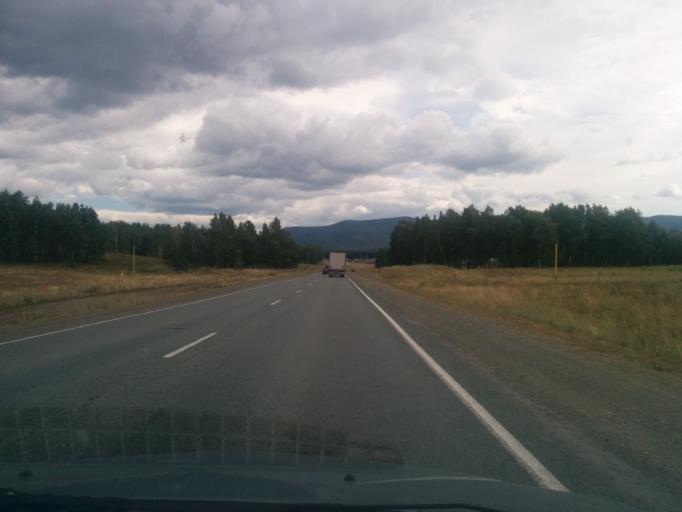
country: RU
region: Bashkortostan
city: Lomovka
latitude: 53.8896
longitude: 58.0960
